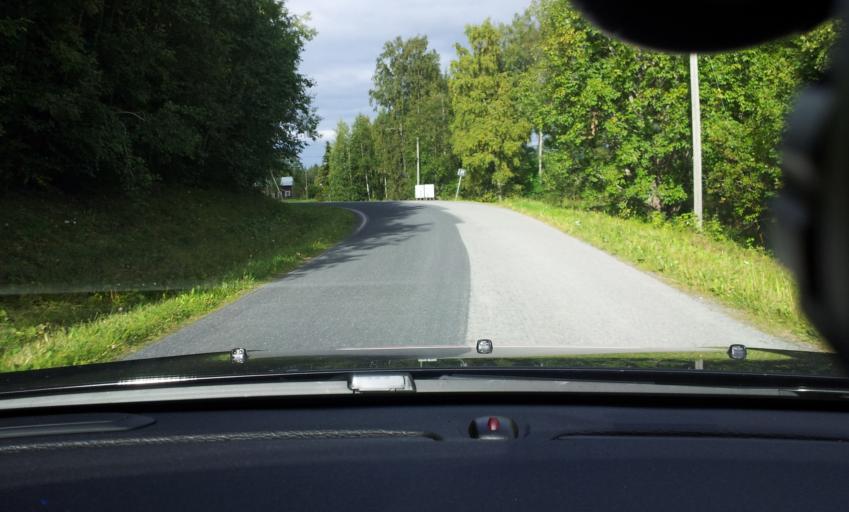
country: SE
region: Jaemtland
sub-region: Krokoms Kommun
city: Valla
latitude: 63.2725
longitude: 13.8942
